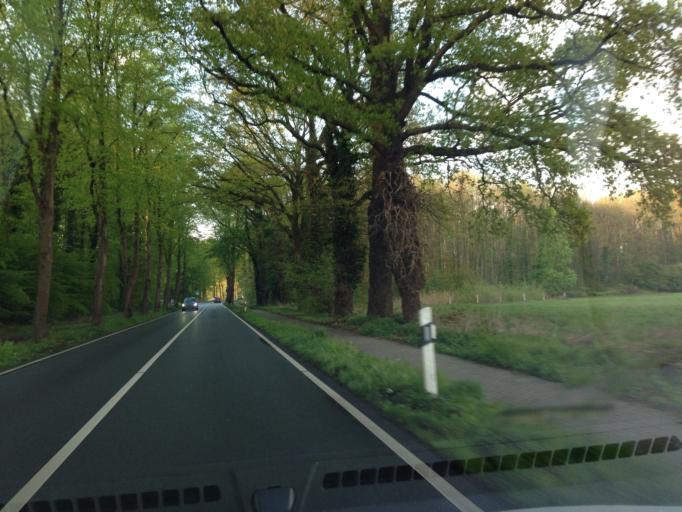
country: DE
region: North Rhine-Westphalia
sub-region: Regierungsbezirk Munster
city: Muenster
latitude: 51.9868
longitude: 7.6789
